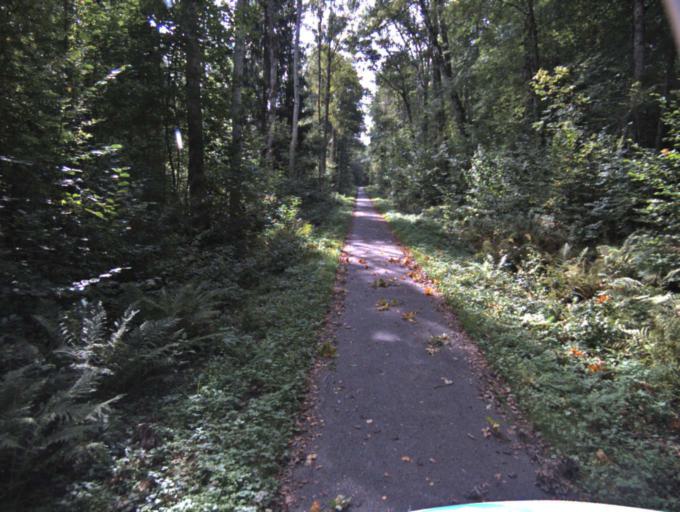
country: SE
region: Vaestra Goetaland
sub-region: Tranemo Kommun
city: Limmared
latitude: 57.6465
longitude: 13.3600
